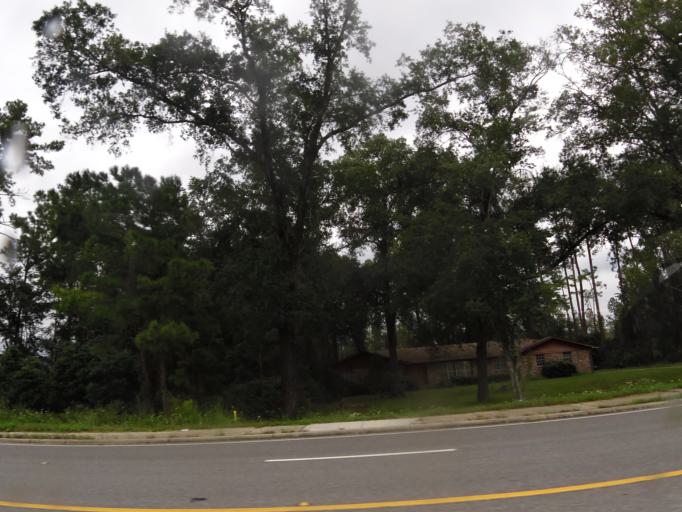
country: US
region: Florida
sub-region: Clay County
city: Middleburg
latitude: 30.1144
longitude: -81.8287
